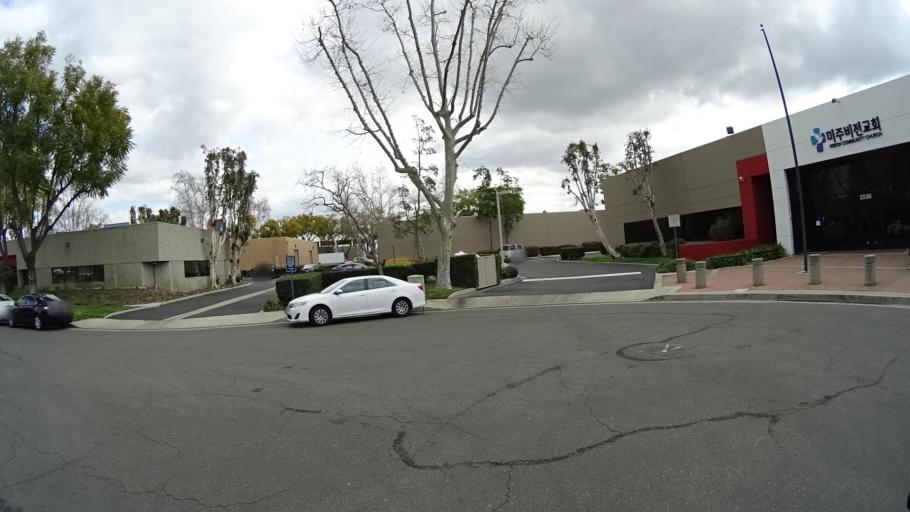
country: US
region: California
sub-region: Orange County
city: Buena Park
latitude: 33.8487
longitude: -117.9735
